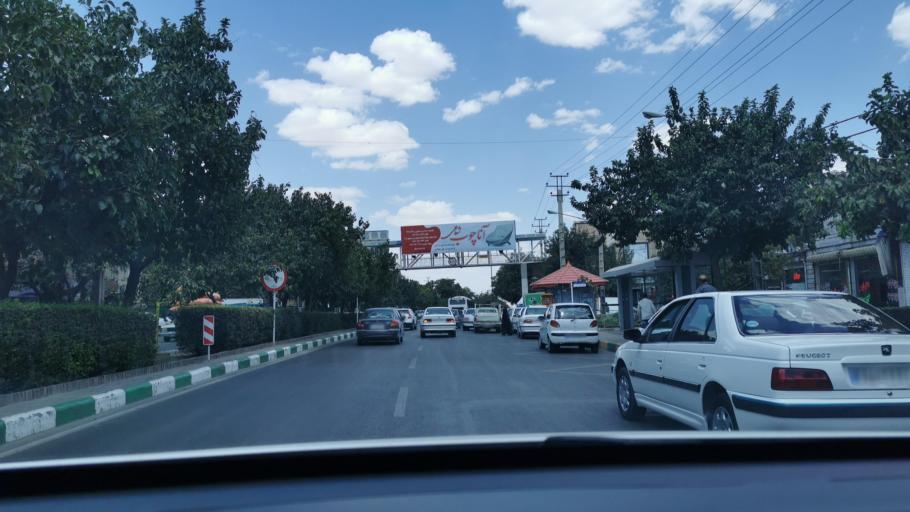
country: IR
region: Razavi Khorasan
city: Mashhad
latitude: 36.3410
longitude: 59.6249
